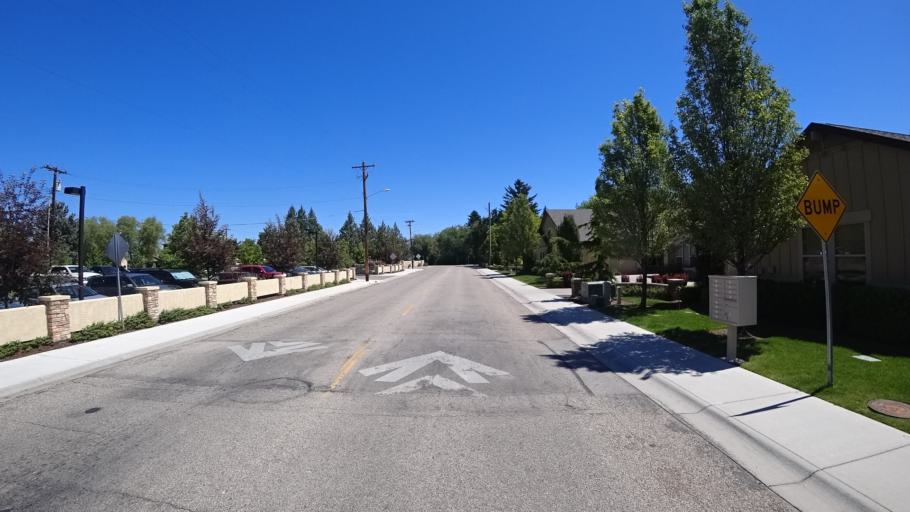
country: US
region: Idaho
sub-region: Ada County
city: Garden City
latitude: 43.5846
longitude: -116.2399
